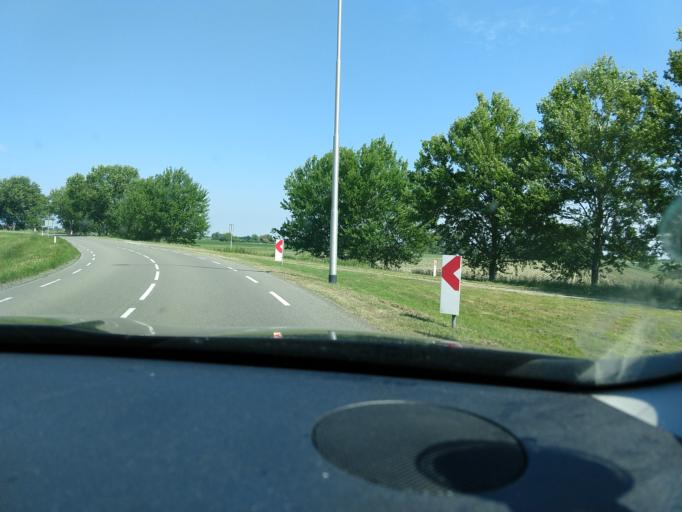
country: NL
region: Zeeland
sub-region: Gemeente Reimerswaal
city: Yerseke
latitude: 51.5766
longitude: 4.0453
